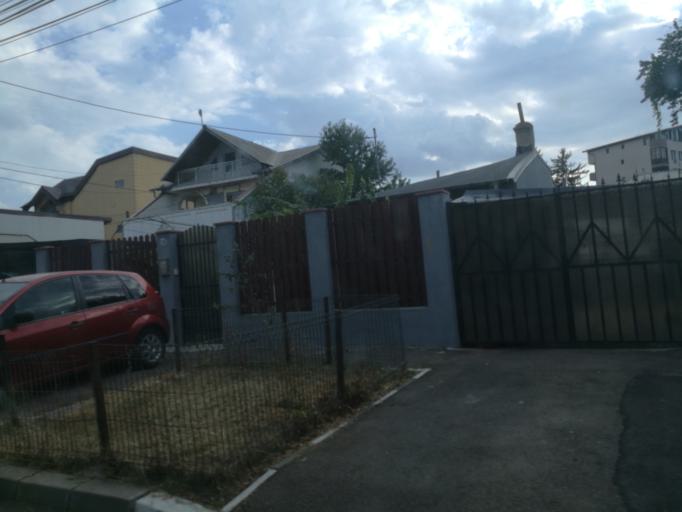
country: RO
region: Ilfov
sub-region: Comuna Chiajna
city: Rosu
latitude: 44.4905
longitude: 26.0529
